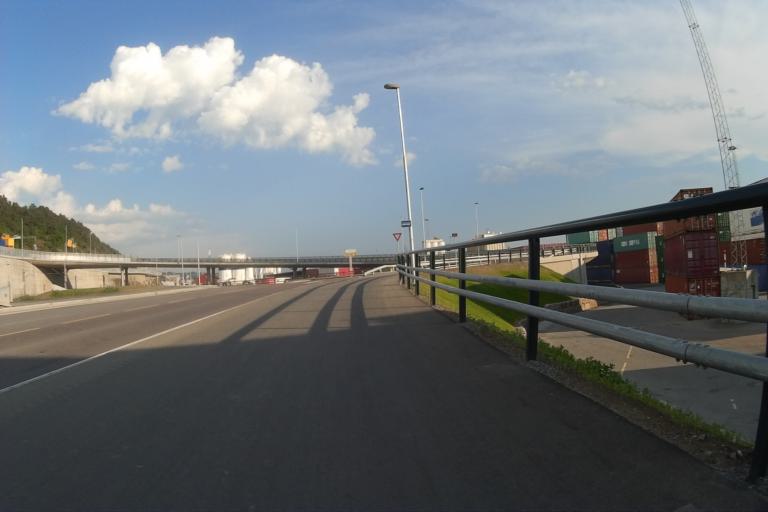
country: NO
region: Oslo
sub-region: Oslo
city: Oslo
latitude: 59.8958
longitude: 10.7559
